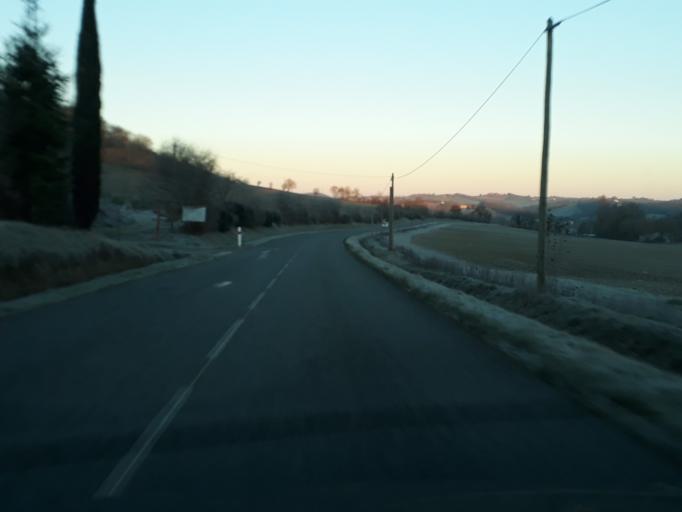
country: FR
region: Midi-Pyrenees
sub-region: Departement du Gers
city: Aubiet
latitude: 43.5830
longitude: 0.7489
